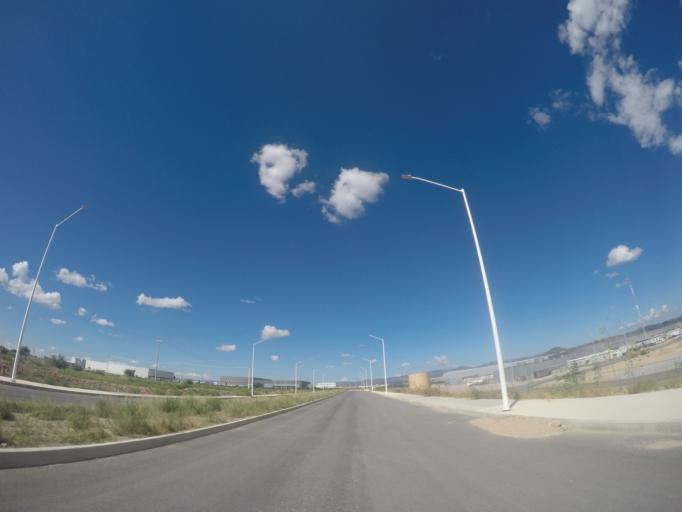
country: MX
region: San Luis Potosi
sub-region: Zaragoza
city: Cerro Gordo
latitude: 21.9683
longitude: -100.8606
